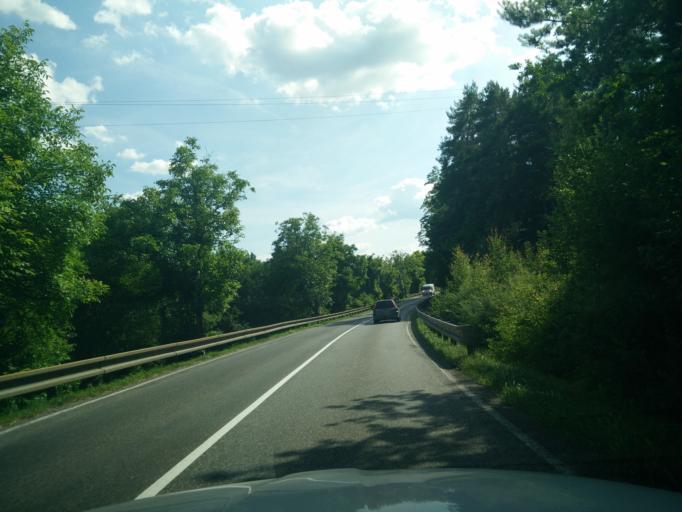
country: SK
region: Nitriansky
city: Prievidza
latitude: 48.8794
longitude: 18.6589
